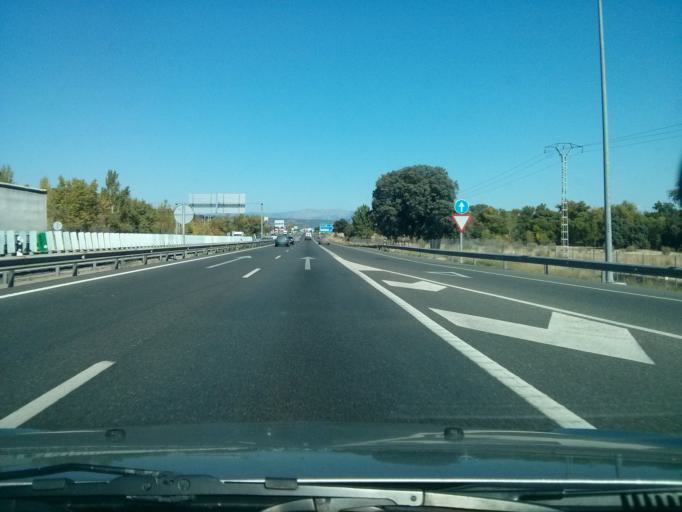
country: ES
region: Madrid
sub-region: Provincia de Madrid
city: San Agustin de Guadalix
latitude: 40.6290
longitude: -3.5882
